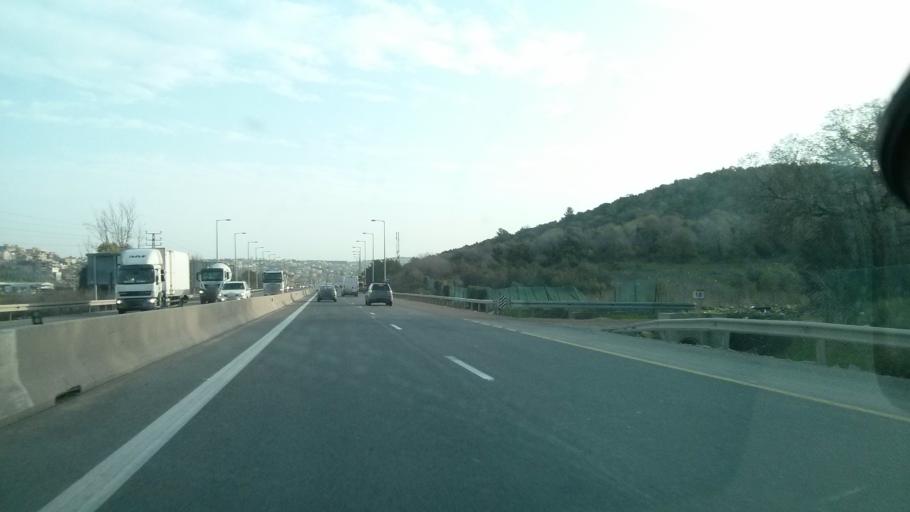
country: PS
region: West Bank
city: Barta`ah ash Sharqiyah
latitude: 32.4942
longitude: 35.0581
